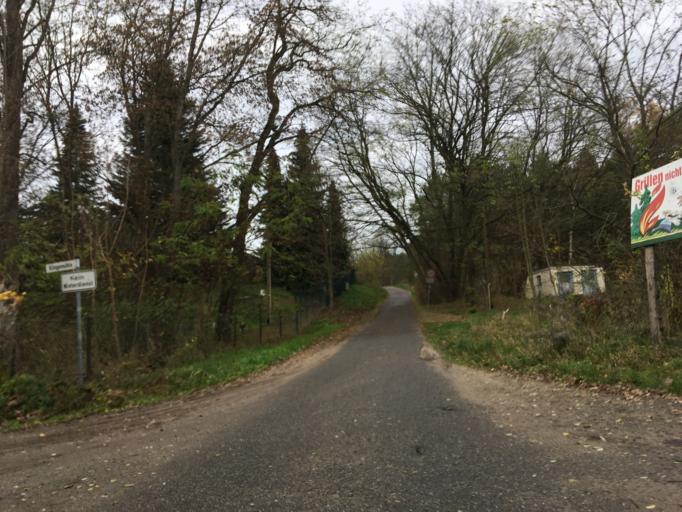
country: DE
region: Brandenburg
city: Mixdorf
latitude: 52.1001
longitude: 14.4331
